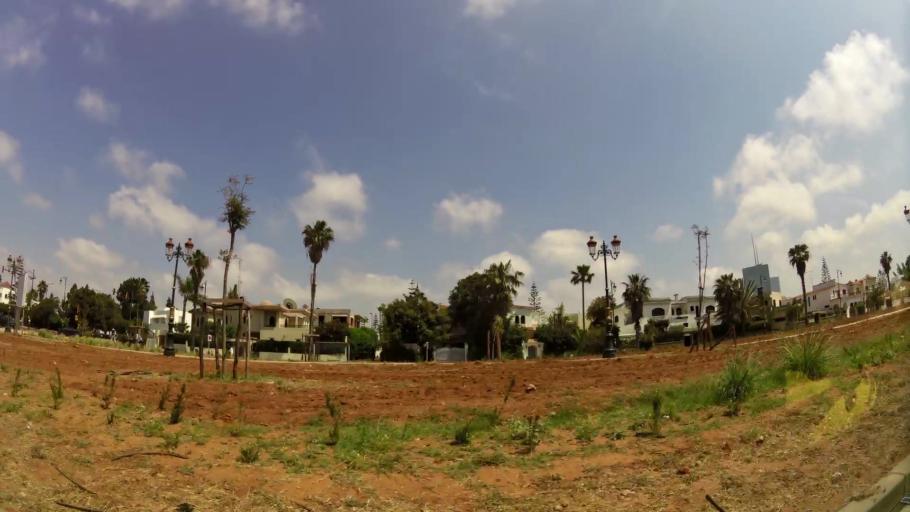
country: MA
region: Rabat-Sale-Zemmour-Zaer
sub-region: Skhirate-Temara
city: Temara
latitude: 33.9642
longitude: -6.8719
